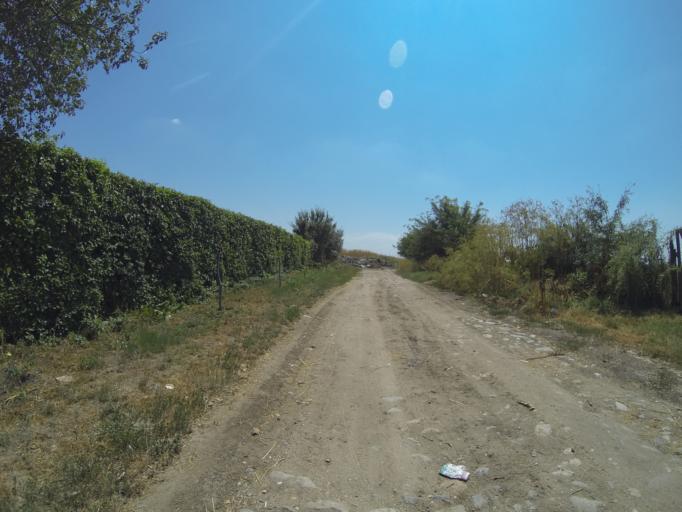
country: RO
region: Dolj
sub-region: Comuna Segarcea
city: Segarcea
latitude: 44.0858
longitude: 23.7400
